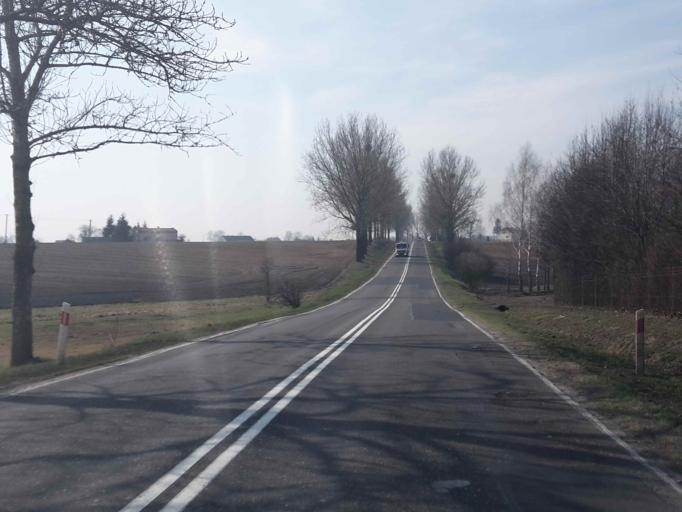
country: PL
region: Kujawsko-Pomorskie
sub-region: Powiat golubsko-dobrzynski
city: Kowalewo Pomorskie
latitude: 53.1379
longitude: 18.8582
